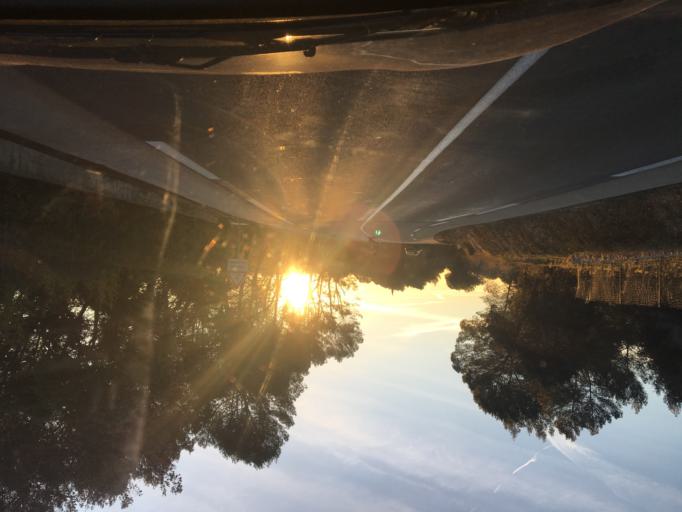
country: FR
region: Provence-Alpes-Cote d'Azur
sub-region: Departement du Var
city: Taradeau
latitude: 43.4618
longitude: 6.4036
